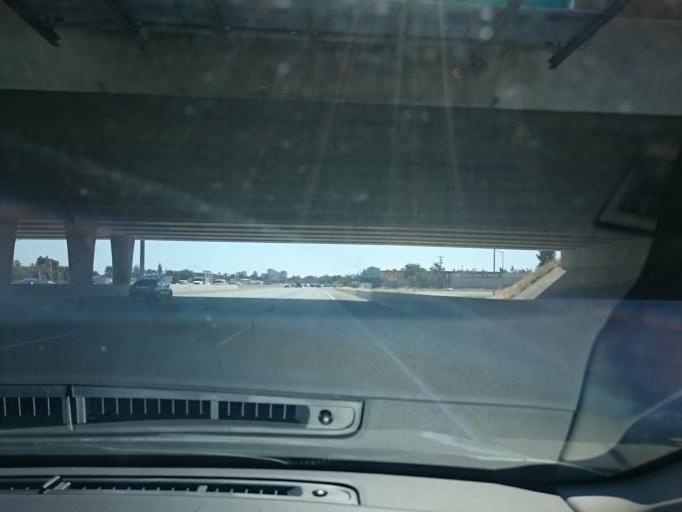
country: US
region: California
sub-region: Yolo County
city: West Sacramento
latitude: 38.5748
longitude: -121.5488
